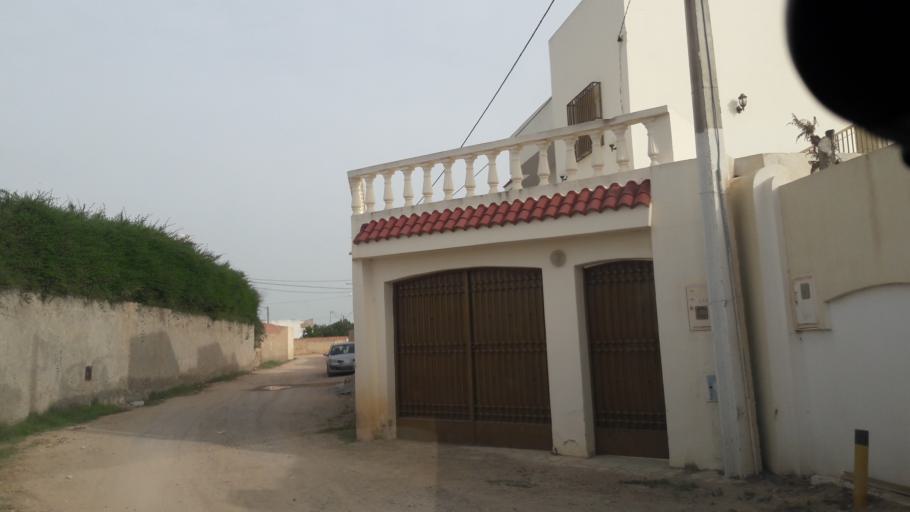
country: TN
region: Safaqis
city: Al Qarmadah
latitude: 34.7789
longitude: 10.7740
